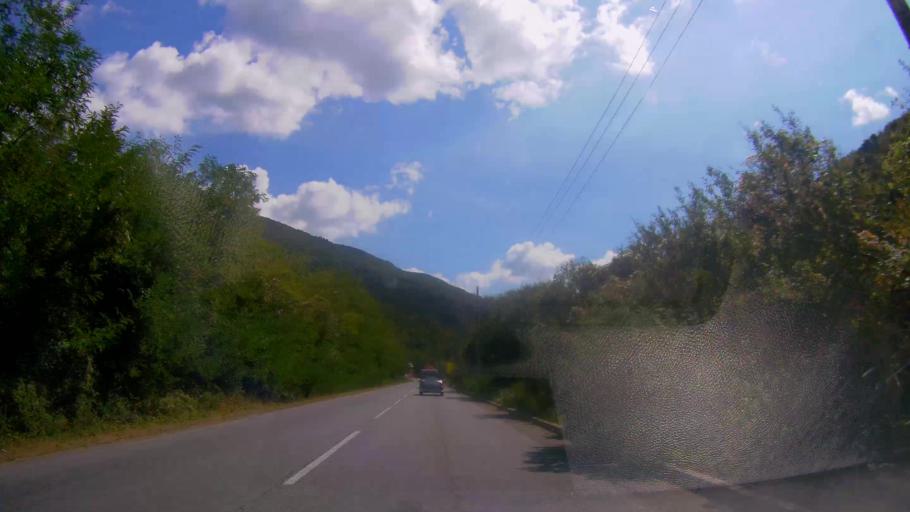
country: BG
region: Stara Zagora
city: Gurkovo
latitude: 42.7351
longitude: 25.7091
